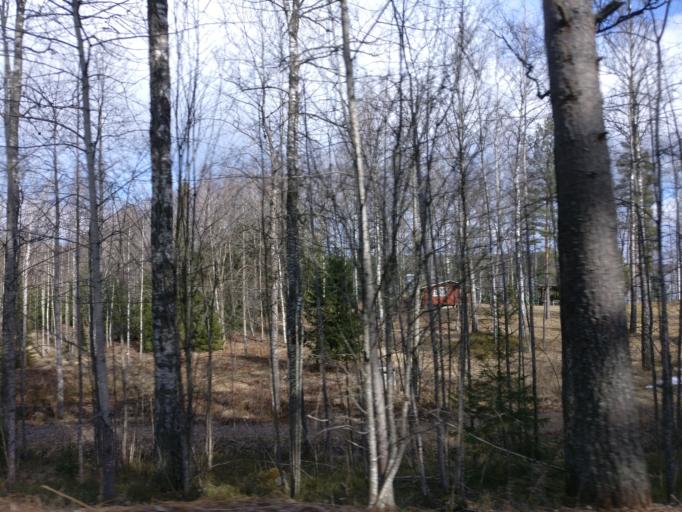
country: FI
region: Varsinais-Suomi
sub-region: Salo
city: Suomusjaervi
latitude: 60.3299
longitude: 23.7040
